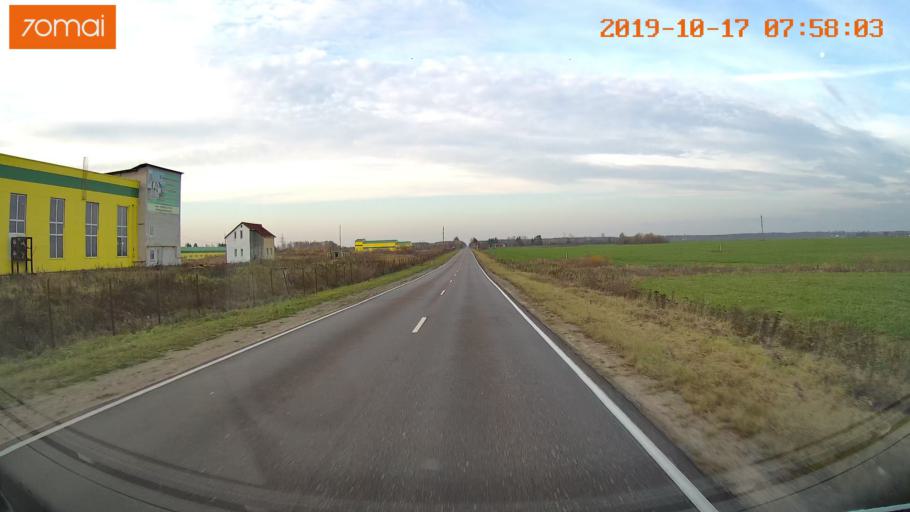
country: RU
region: Vladimir
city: Bavleny
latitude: 56.4063
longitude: 39.5650
